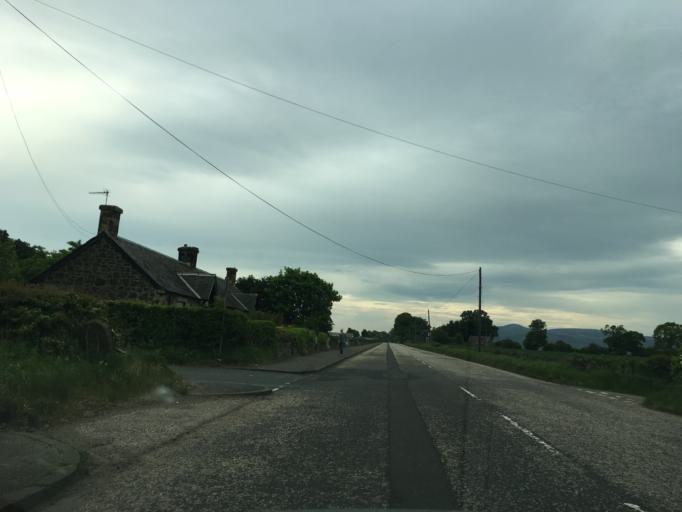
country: GB
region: Scotland
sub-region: Edinburgh
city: Currie
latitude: 55.9471
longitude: -3.3283
